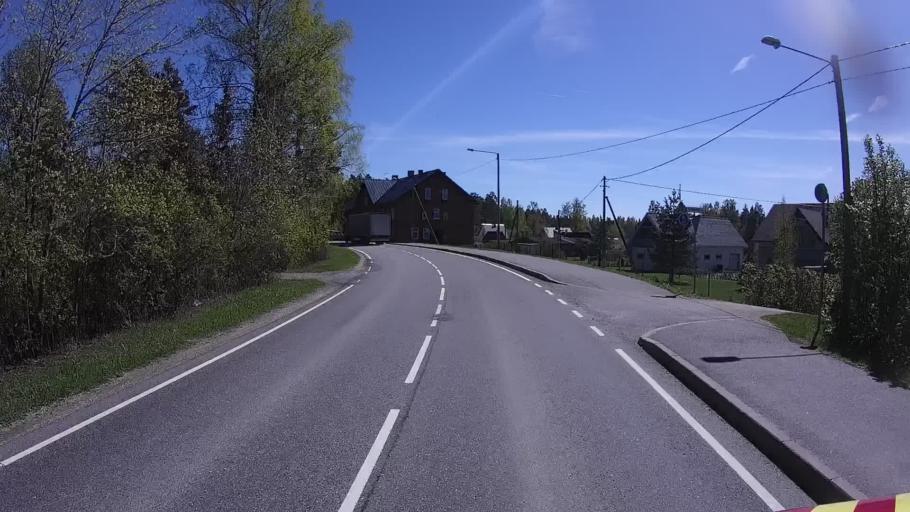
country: EE
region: Harju
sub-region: Kuusalu vald
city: Kuusalu
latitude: 59.2827
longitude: 25.6135
